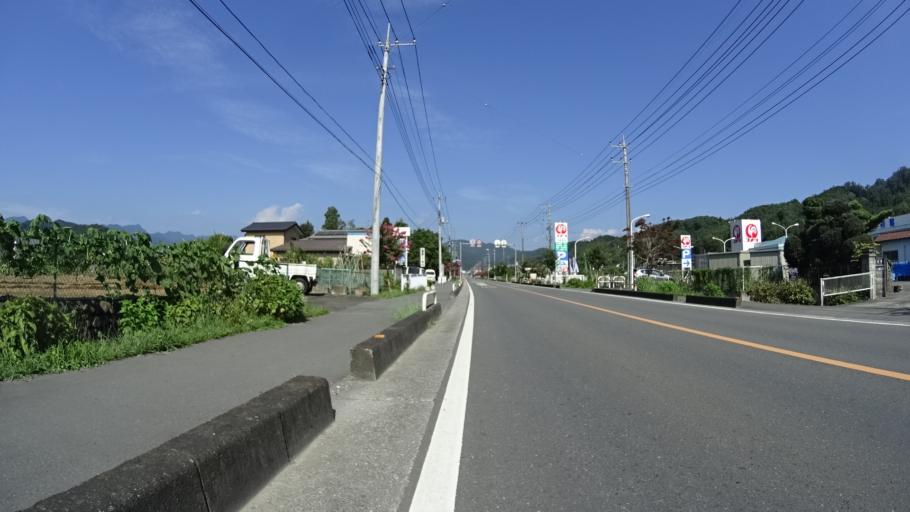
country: JP
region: Saitama
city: Chichibu
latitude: 36.0226
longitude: 139.0053
